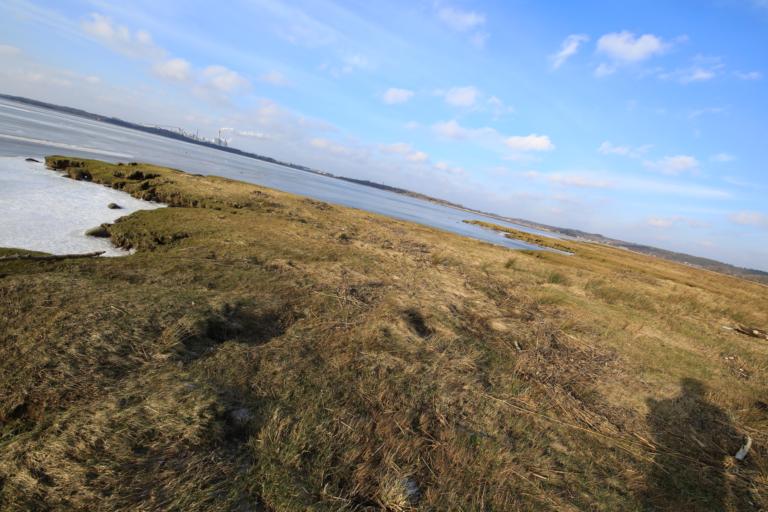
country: SE
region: Halland
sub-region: Kungsbacka Kommun
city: Frillesas
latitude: 57.2145
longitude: 12.2155
